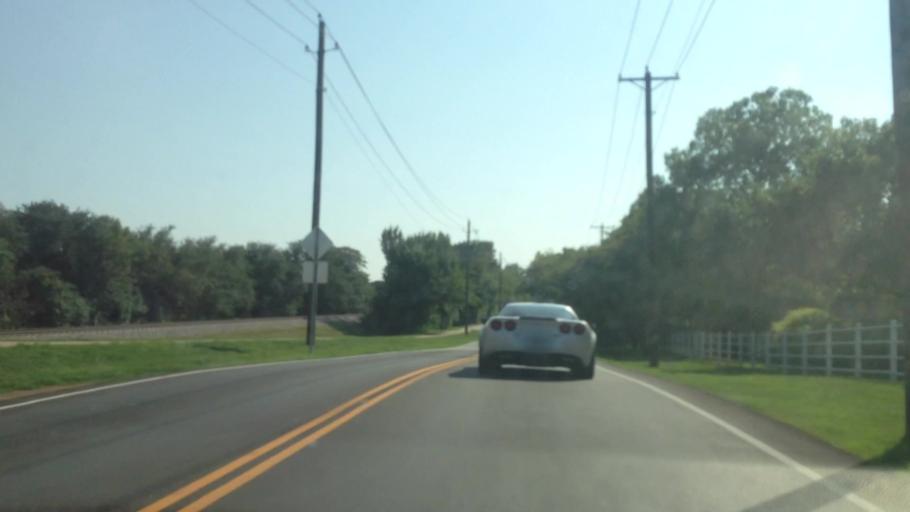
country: US
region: Texas
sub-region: Tarrant County
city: Colleyville
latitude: 32.9018
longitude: -97.1572
